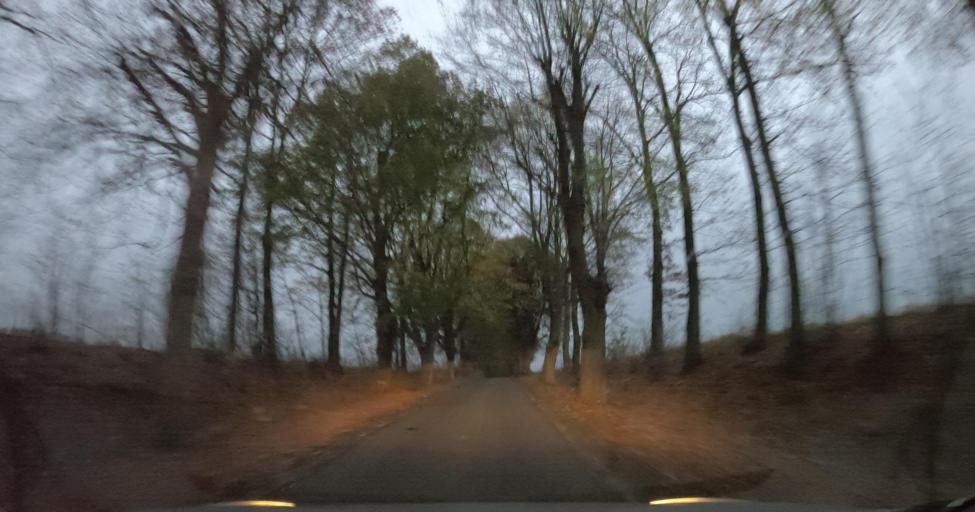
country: PL
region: West Pomeranian Voivodeship
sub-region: Powiat bialogardzki
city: Tychowo
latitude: 53.8373
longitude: 16.2353
